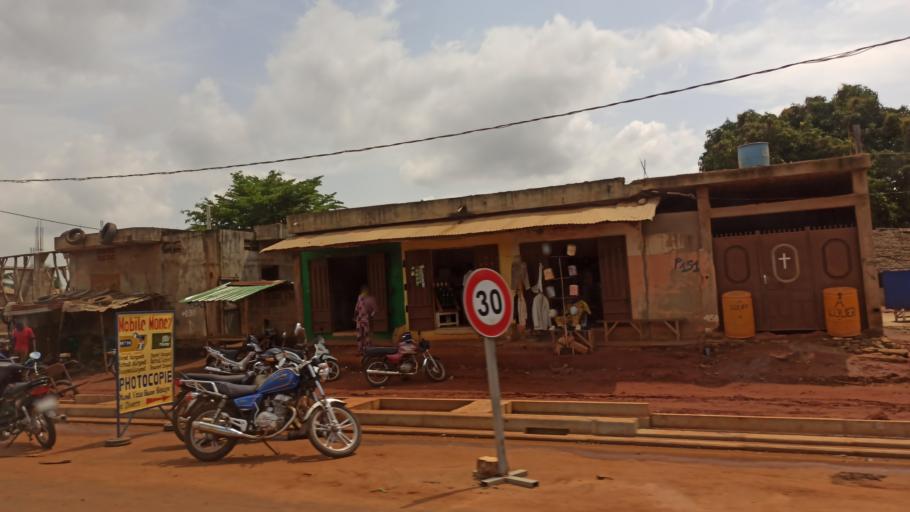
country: BJ
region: Queme
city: Porto-Novo
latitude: 6.4963
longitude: 2.5905
